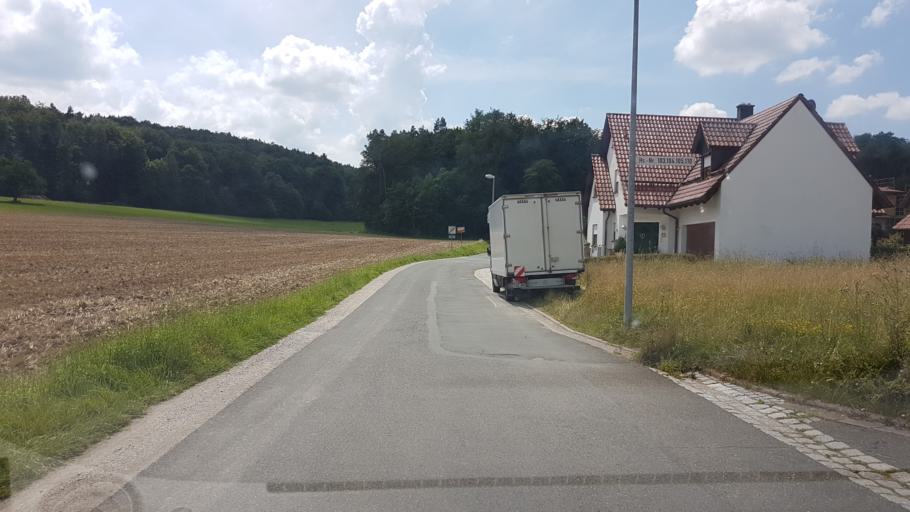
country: DE
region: Bavaria
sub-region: Upper Franconia
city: Gossweinstein
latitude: 49.7765
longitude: 11.2866
